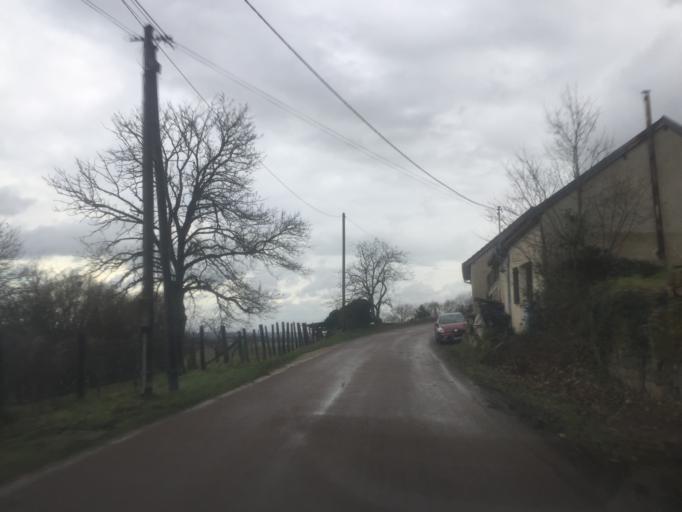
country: FR
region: Franche-Comte
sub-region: Departement de la Haute-Saone
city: Pesmes
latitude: 47.2243
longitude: 5.5365
